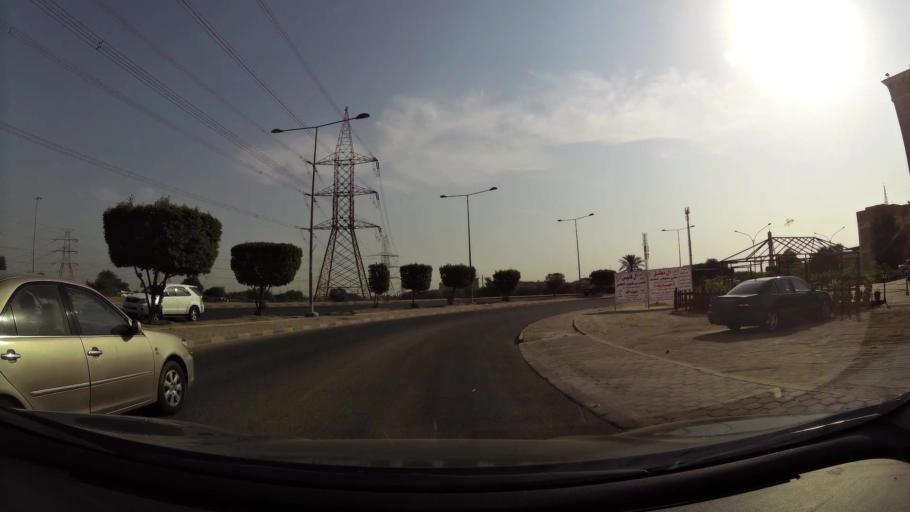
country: KW
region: Mubarak al Kabir
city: Mubarak al Kabir
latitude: 29.1725
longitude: 48.0597
